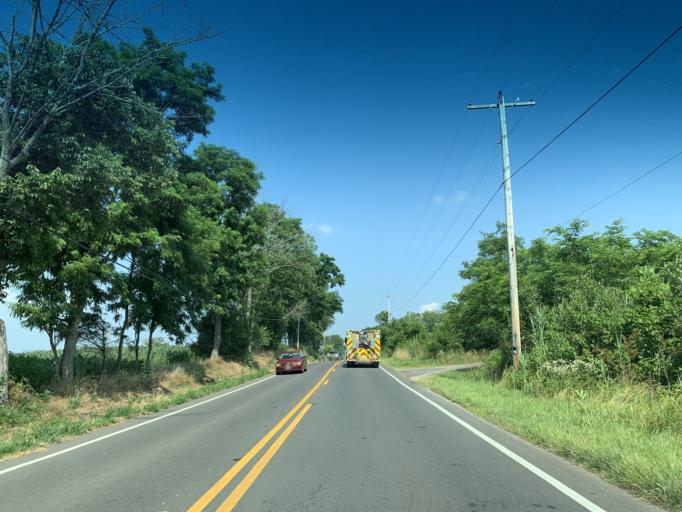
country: US
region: Maryland
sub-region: Montgomery County
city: Poolesville
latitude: 39.1324
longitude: -77.3945
